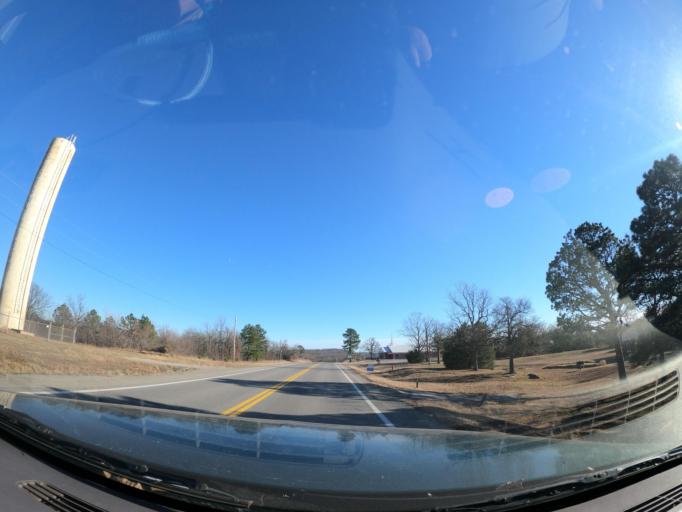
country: US
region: Oklahoma
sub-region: Pittsburg County
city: Longtown
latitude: 35.2293
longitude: -95.4523
